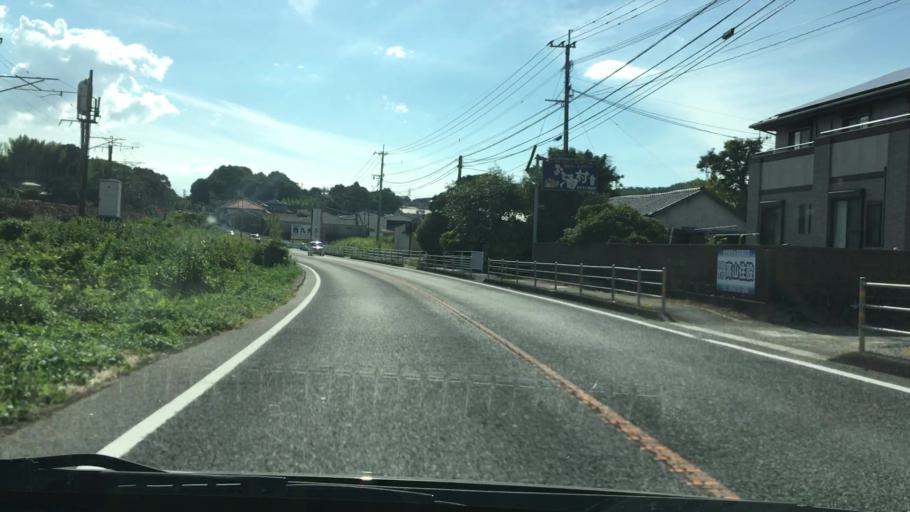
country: JP
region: Nagasaki
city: Sasebo
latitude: 33.1450
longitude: 129.8193
